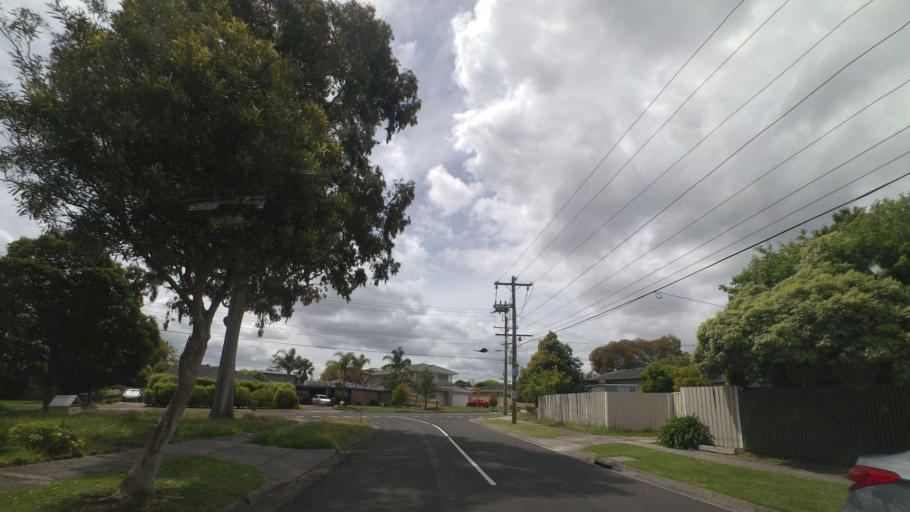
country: AU
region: Victoria
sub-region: Knox
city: Knoxfield
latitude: -37.8901
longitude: 145.2425
